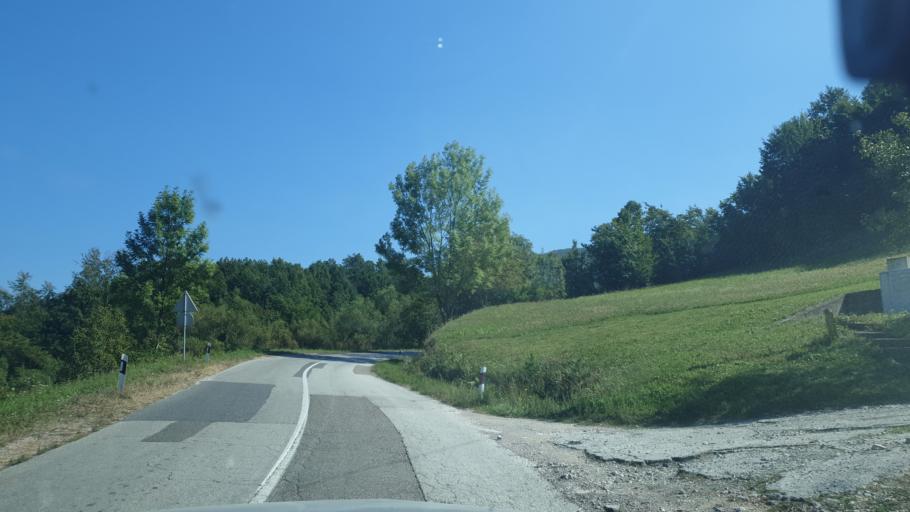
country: RS
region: Central Serbia
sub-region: Kolubarski Okrug
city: Mionica
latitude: 44.1599
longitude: 19.9847
